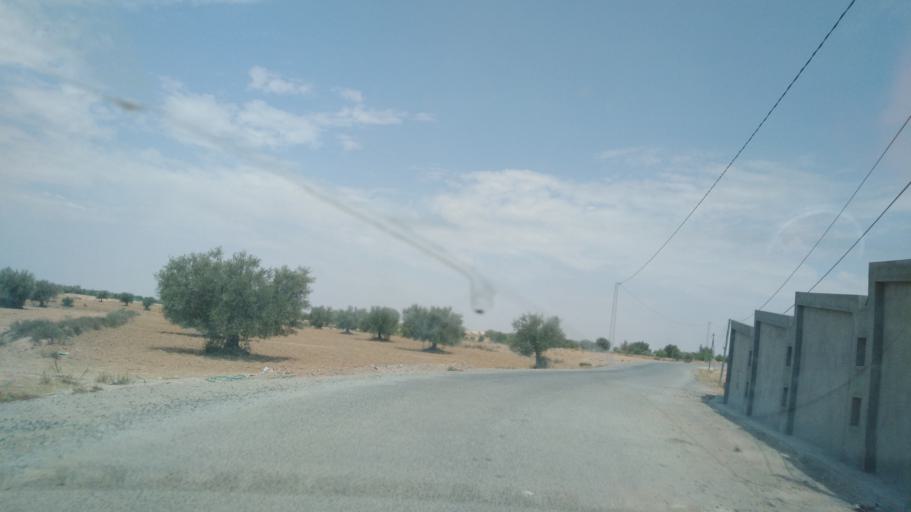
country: TN
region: Safaqis
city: Sfax
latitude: 34.7448
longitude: 10.5603
